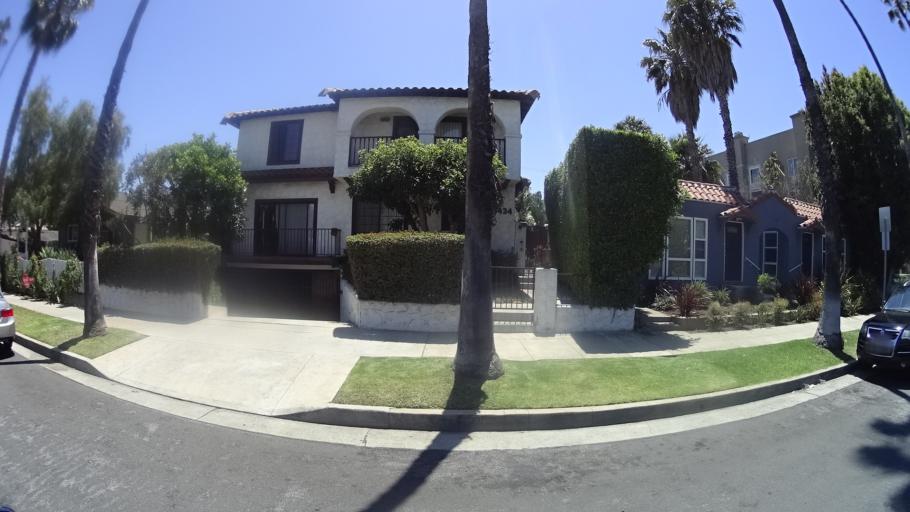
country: US
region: California
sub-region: Los Angeles County
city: Santa Monica
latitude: 34.0272
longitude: -118.4802
